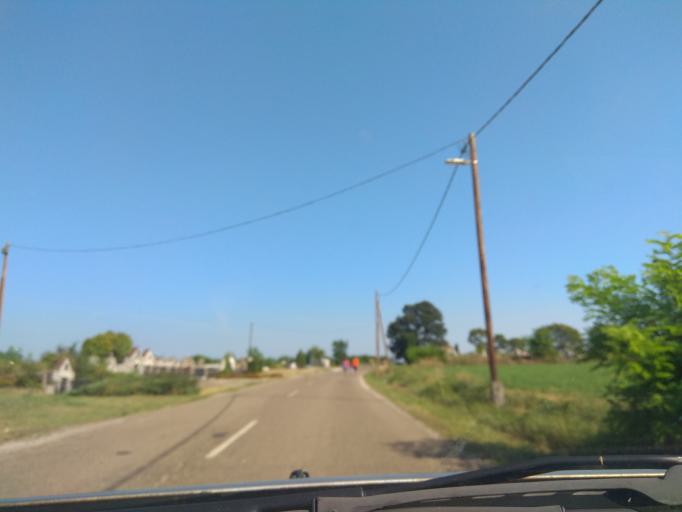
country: HU
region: Borsod-Abauj-Zemplen
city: Emod
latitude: 47.9498
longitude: 20.8105
